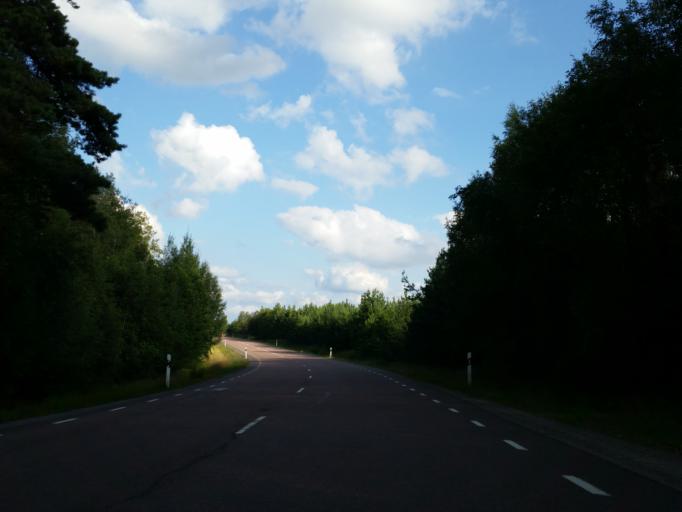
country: SE
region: Stockholm
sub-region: Nykvarns Kommun
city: Nykvarn
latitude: 59.2139
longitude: 17.3234
